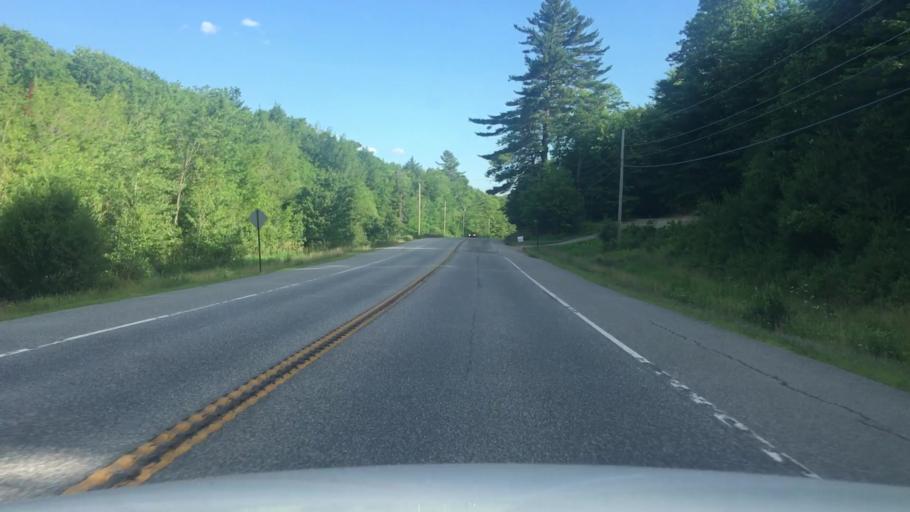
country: US
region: Maine
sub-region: Androscoggin County
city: Livermore
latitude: 44.4193
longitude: -70.2205
